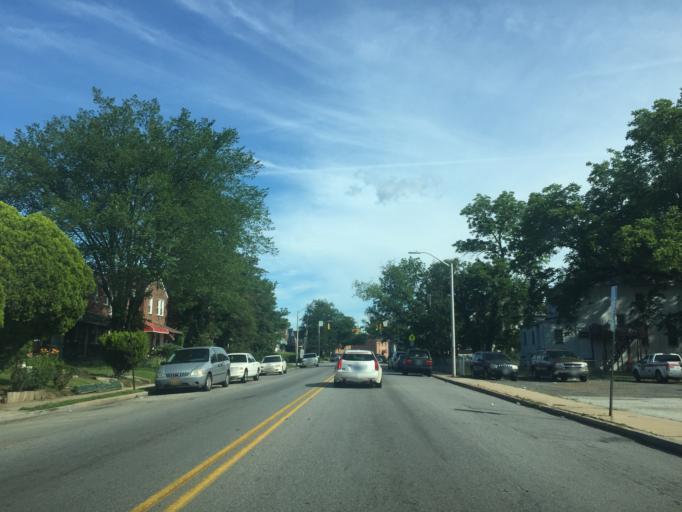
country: US
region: Maryland
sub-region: Baltimore County
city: Lochearn
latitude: 39.3343
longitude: -76.6837
